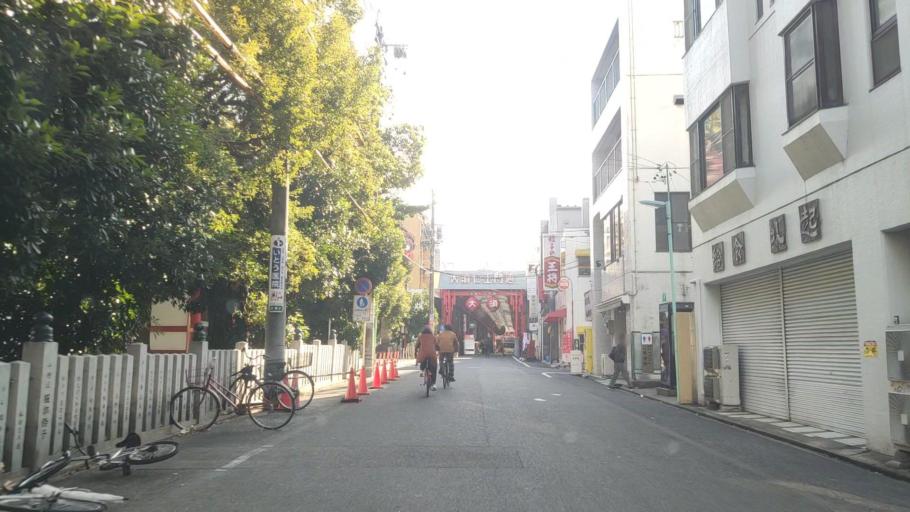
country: JP
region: Aichi
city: Nagoya-shi
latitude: 35.1592
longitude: 136.8990
